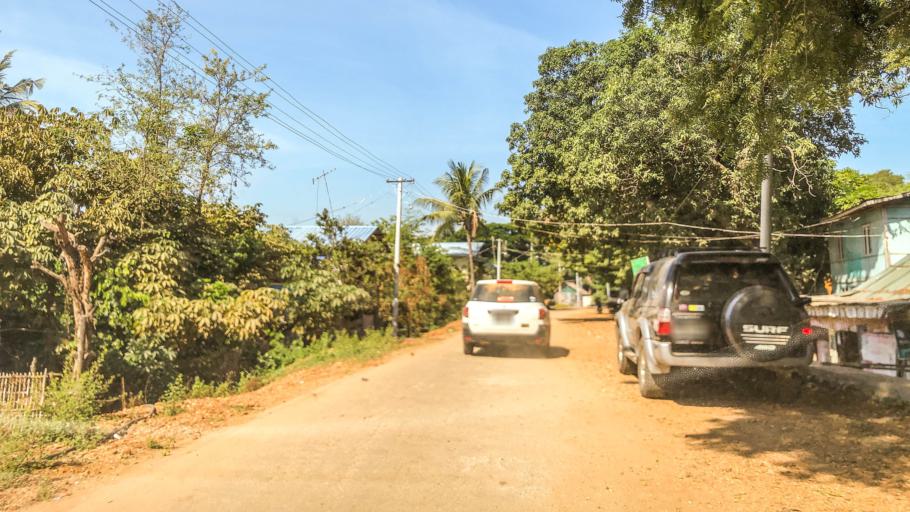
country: MM
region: Magway
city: Magway
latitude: 19.9713
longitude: 95.0421
